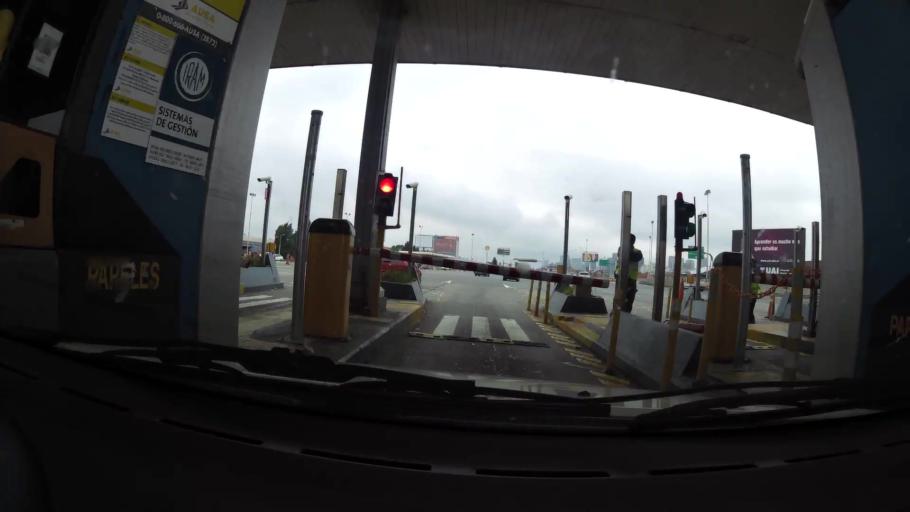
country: AR
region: Buenos Aires F.D.
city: Retiro
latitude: -34.5753
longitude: -58.3932
